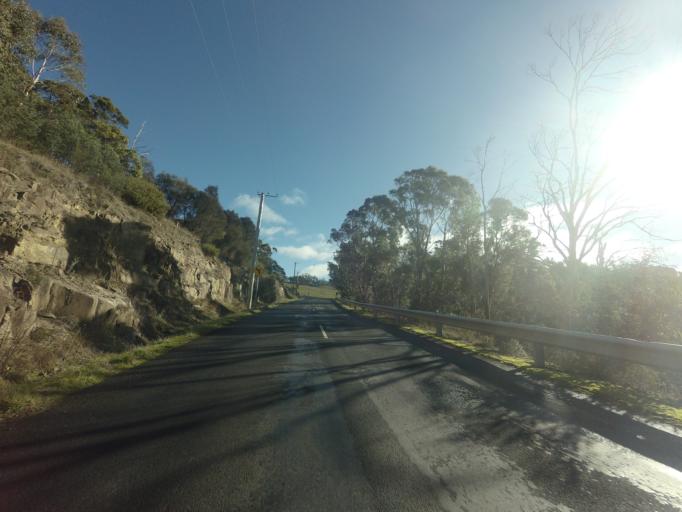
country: AU
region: Tasmania
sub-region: Glenorchy
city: Berriedale
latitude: -42.8227
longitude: 147.2052
